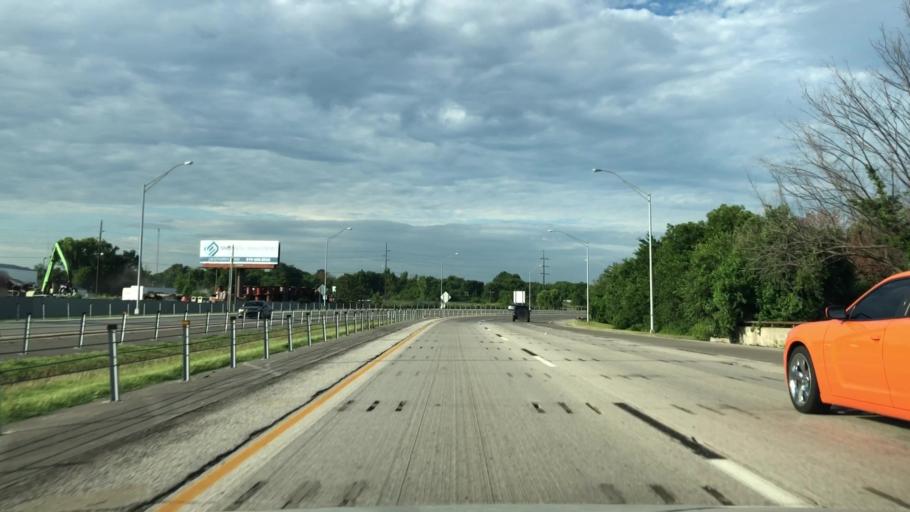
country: US
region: Oklahoma
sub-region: Tulsa County
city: Tulsa
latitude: 36.1873
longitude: -95.9604
